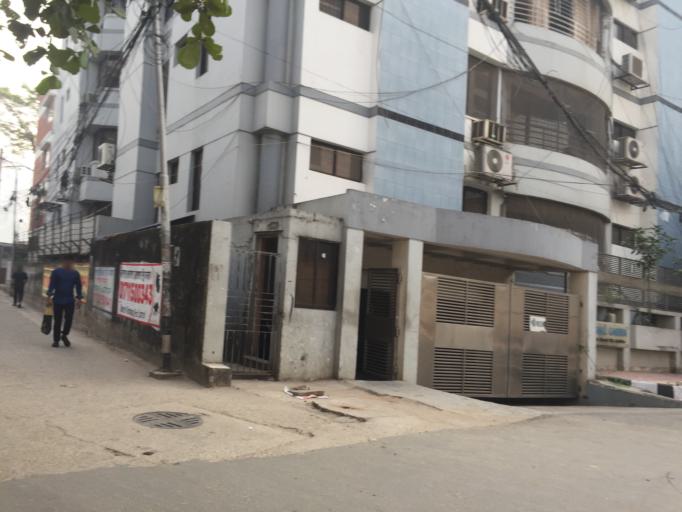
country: BD
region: Dhaka
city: Paltan
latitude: 23.7890
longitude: 90.4207
